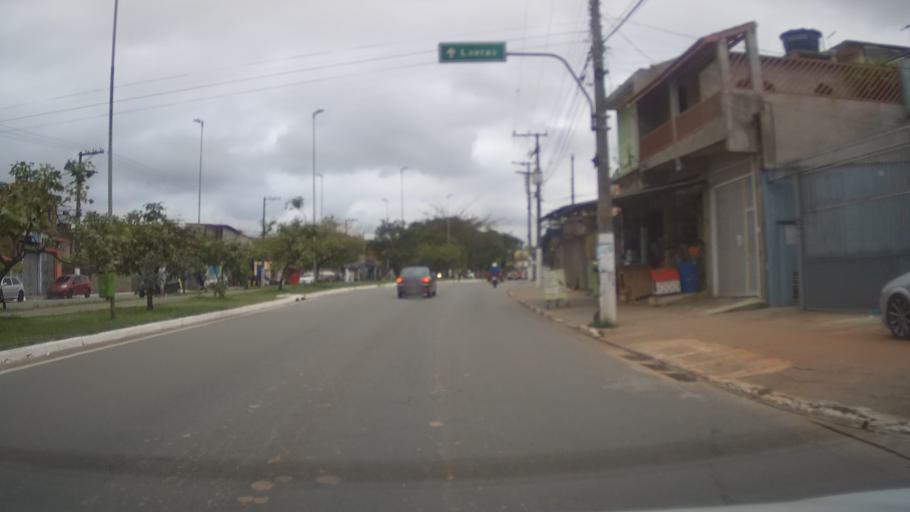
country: BR
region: Sao Paulo
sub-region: Guarulhos
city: Guarulhos
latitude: -23.4091
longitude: -46.4514
